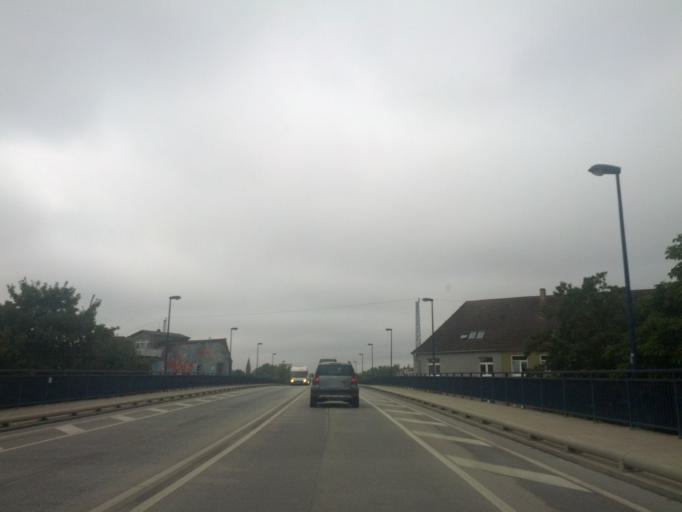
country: DE
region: Mecklenburg-Vorpommern
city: Wismar
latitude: 53.8933
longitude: 11.4755
